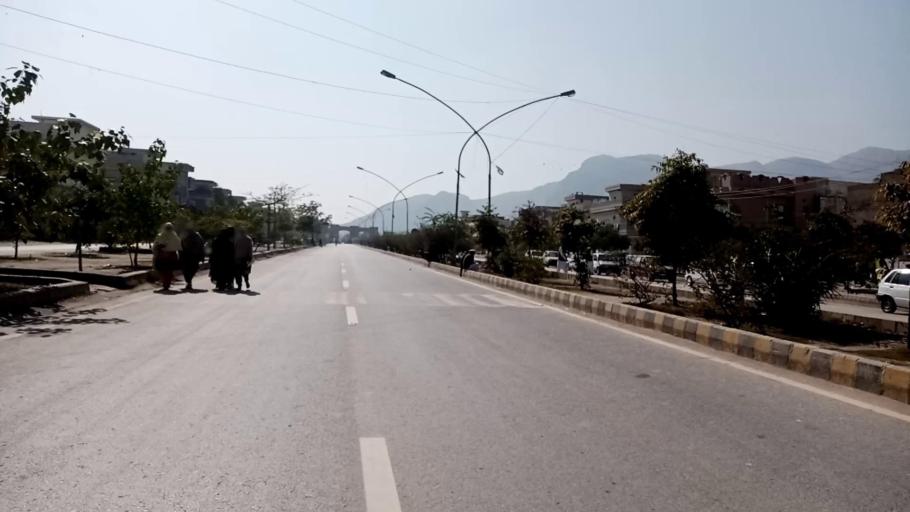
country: PK
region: Khyber Pakhtunkhwa
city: Peshawar
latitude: 33.9511
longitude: 71.4329
